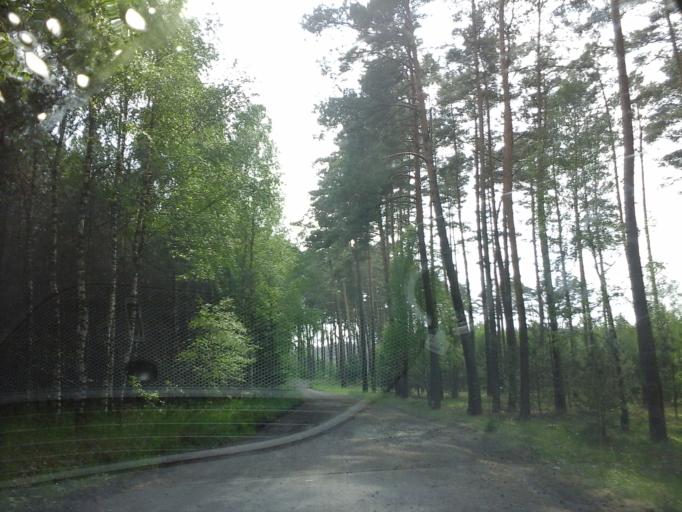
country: PL
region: West Pomeranian Voivodeship
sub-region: Powiat walecki
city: Tuczno
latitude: 53.2197
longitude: 16.0262
